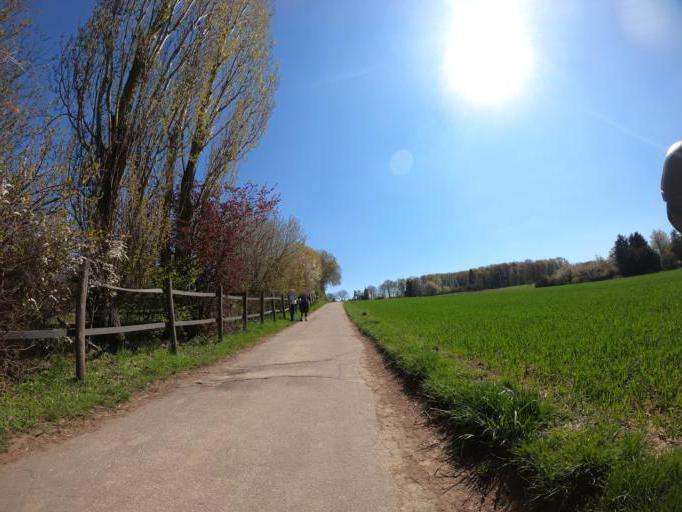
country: DE
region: Baden-Wuerttemberg
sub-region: Karlsruhe Region
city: Eutingen
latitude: 48.9082
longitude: 8.7277
